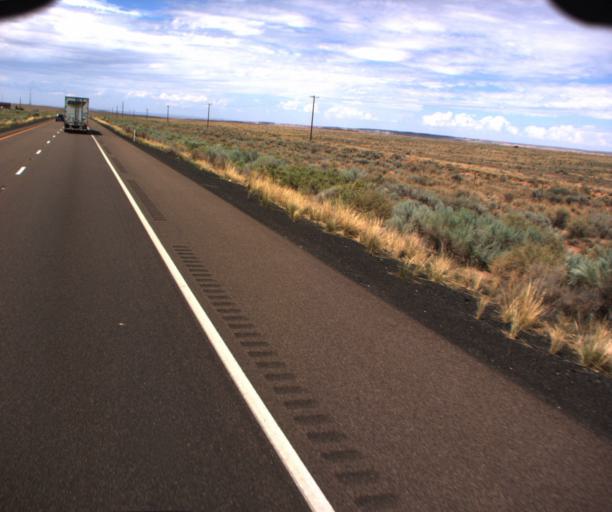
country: US
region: Arizona
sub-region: Navajo County
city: Holbrook
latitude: 35.0400
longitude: -109.8172
